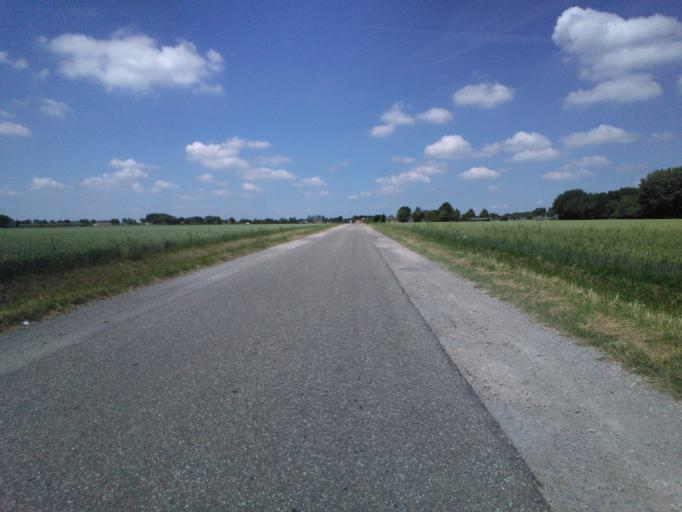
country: NL
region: North Brabant
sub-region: Gemeente Woudrichem
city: Woudrichem
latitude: 51.7996
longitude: 4.9879
